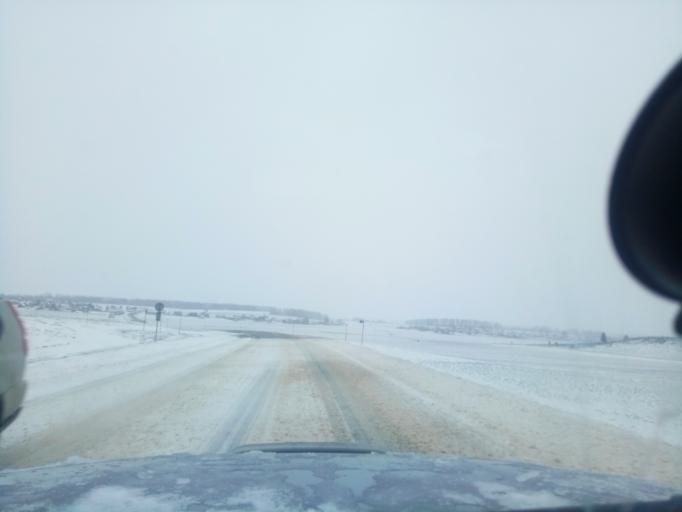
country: BY
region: Minsk
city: Haradzyeya
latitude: 53.3328
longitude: 26.5273
